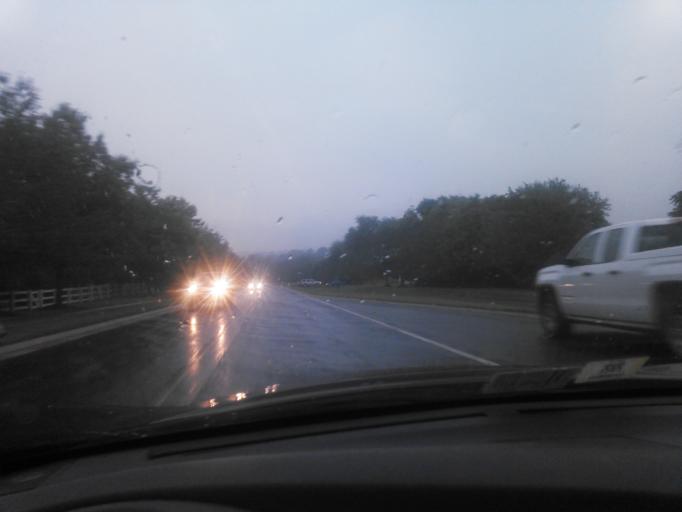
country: US
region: Virginia
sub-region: Loudoun County
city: Purcellville
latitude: 39.1395
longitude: -77.7637
